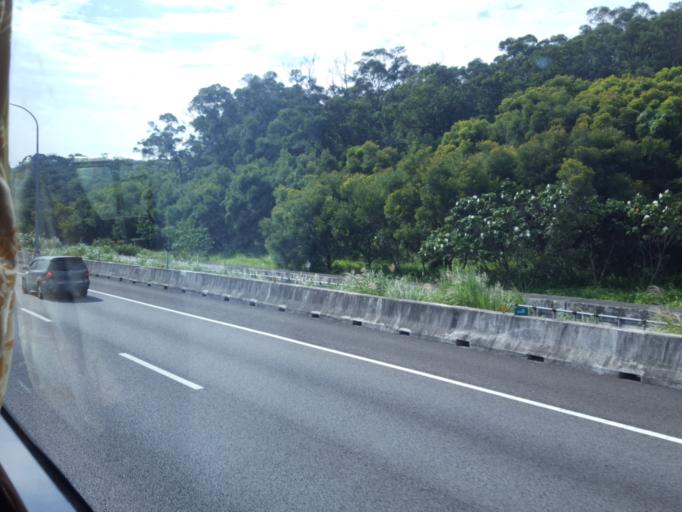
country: TW
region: Taiwan
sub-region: Taoyuan
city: Taoyuan
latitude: 25.0595
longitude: 121.3312
